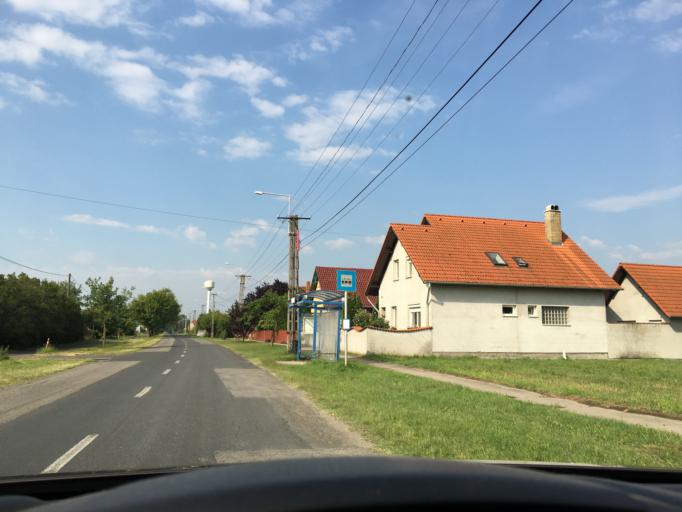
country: HU
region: Csongrad
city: Morahalom
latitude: 46.2118
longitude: 19.8892
